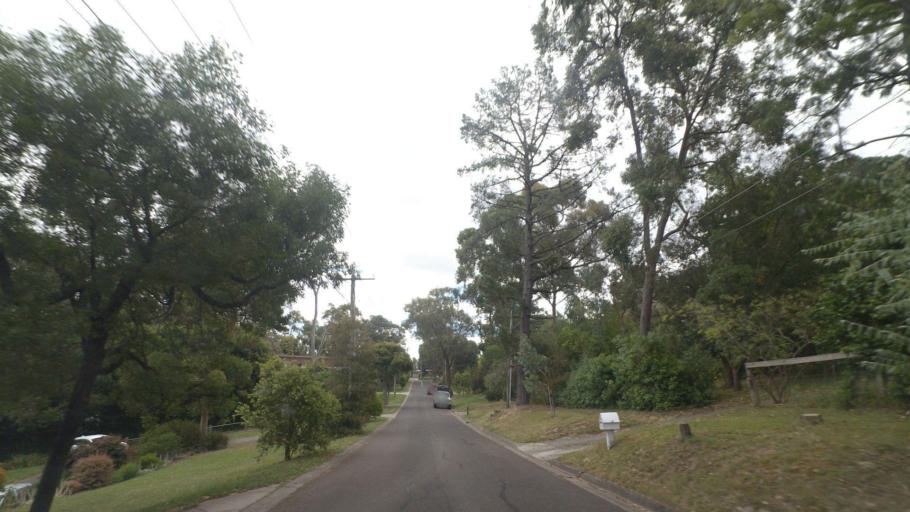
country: AU
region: Victoria
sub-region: Maroondah
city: Warranwood
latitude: -37.7731
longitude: 145.2504
